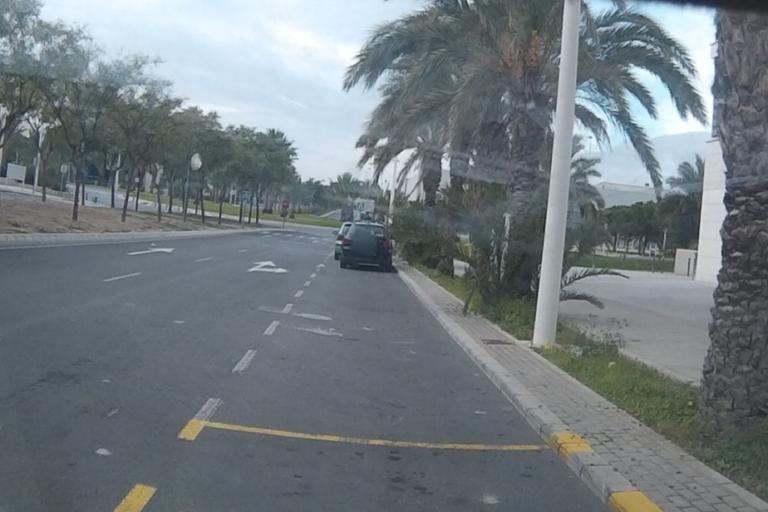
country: ES
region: Valencia
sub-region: Provincia de Alicante
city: Elche
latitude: 38.2929
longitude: -0.6120
